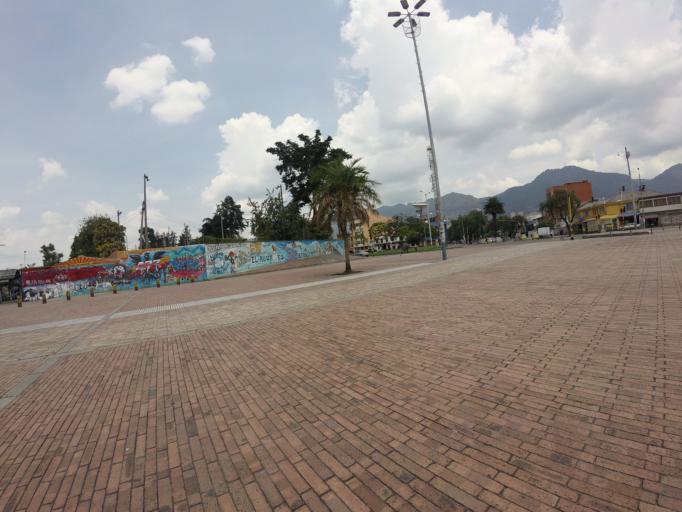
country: CO
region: Bogota D.C.
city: Bogota
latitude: 4.6460
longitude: -74.0760
